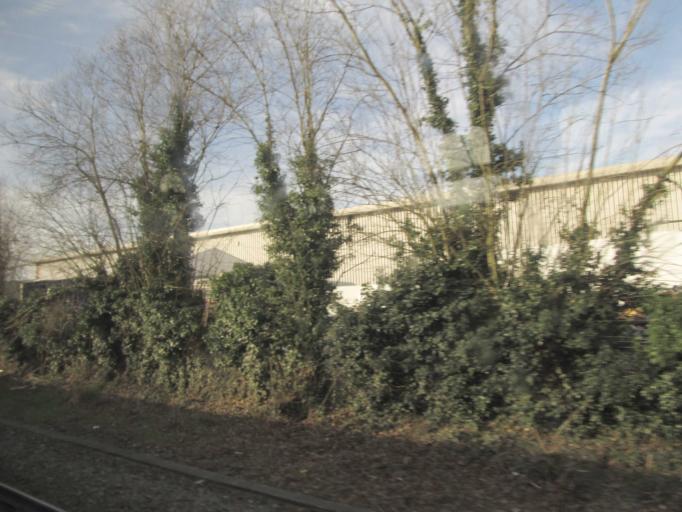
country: GB
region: England
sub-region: Hampshire
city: Farnborough
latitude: 51.2779
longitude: -0.7320
